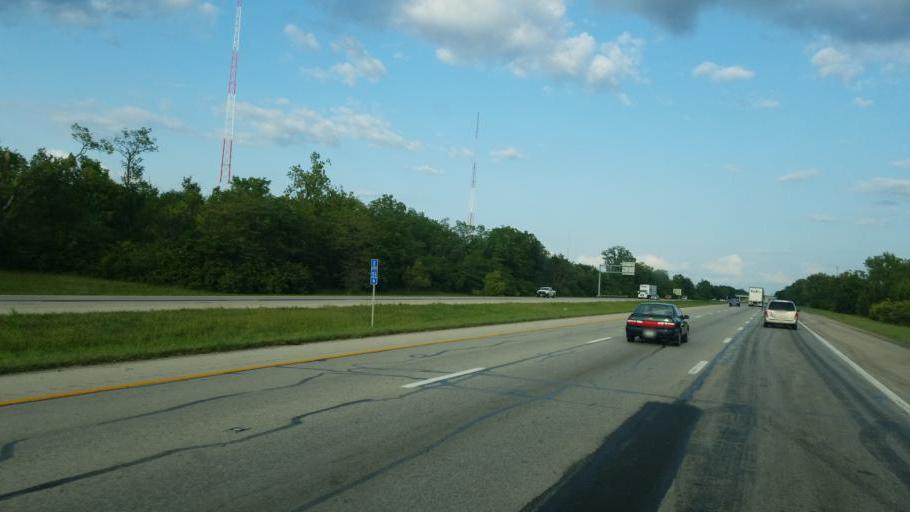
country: US
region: Ohio
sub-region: Franklin County
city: Obetz
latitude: 39.8732
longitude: -82.9828
